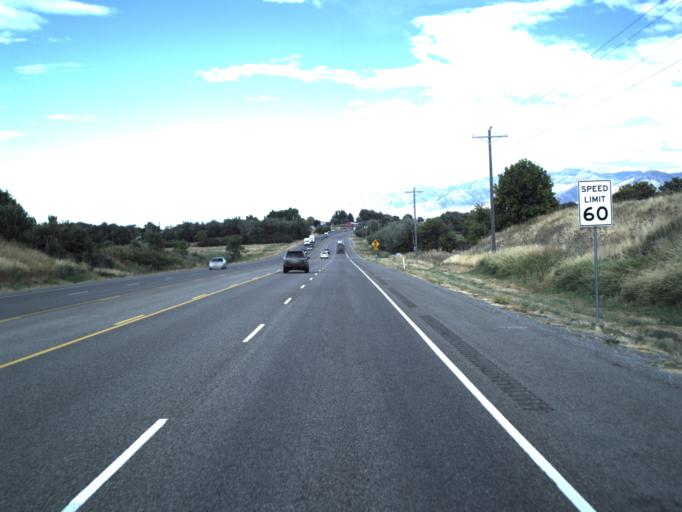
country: US
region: Utah
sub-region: Cache County
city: Wellsville
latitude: 41.6368
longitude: -111.9193
